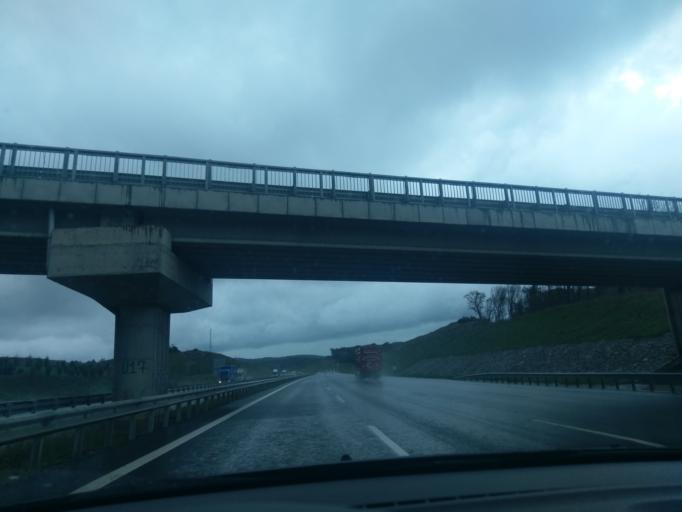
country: TR
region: Istanbul
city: Kemerburgaz
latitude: 41.2328
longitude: 28.9239
